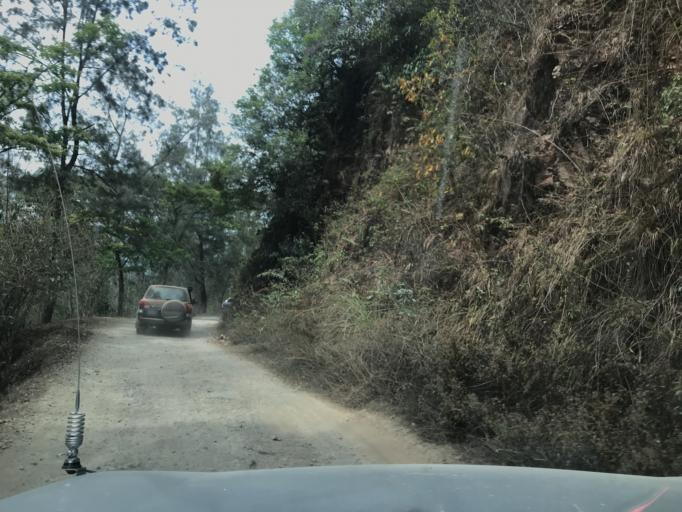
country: TL
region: Ermera
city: Gleno
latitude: -8.8224
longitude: 125.4334
